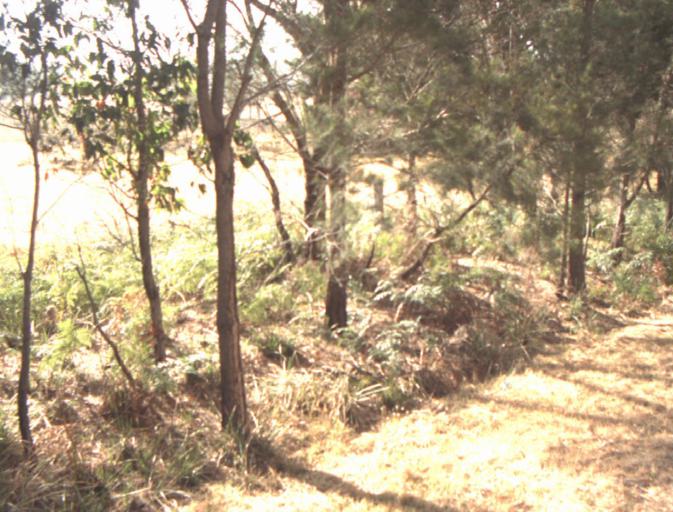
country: AU
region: Tasmania
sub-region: Dorset
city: Bridport
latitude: -41.1092
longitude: 147.2002
